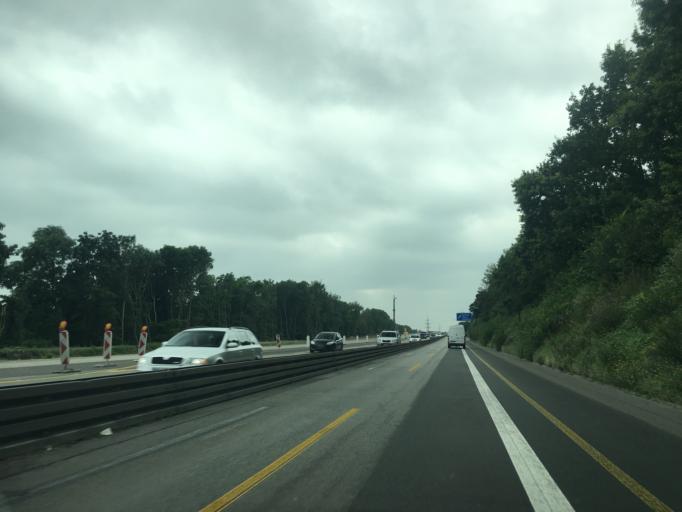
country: DE
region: North Rhine-Westphalia
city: Meiderich
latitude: 51.4845
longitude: 6.7402
